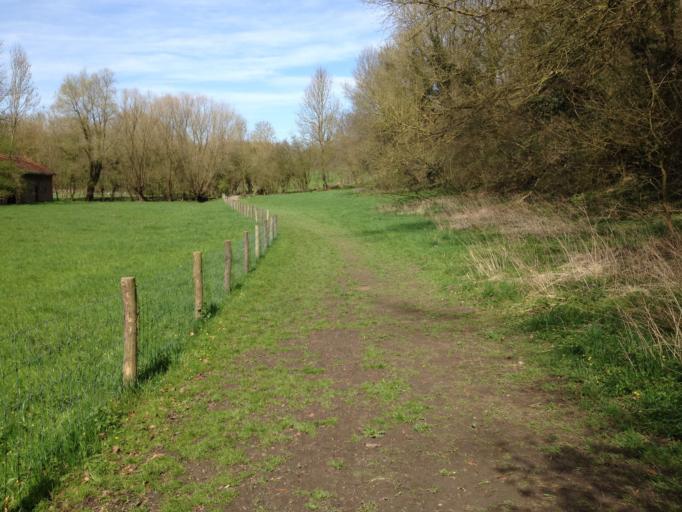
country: NL
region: Limburg
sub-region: Eijsden-Margraten
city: Margraten
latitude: 50.7809
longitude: 5.8576
